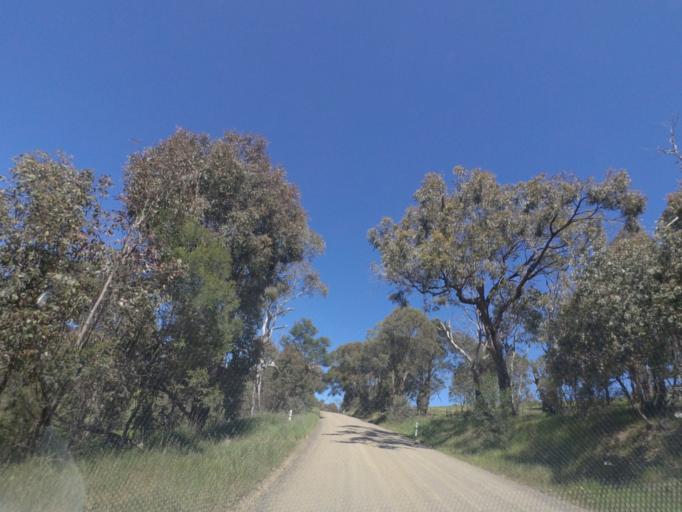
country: AU
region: Victoria
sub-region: Whittlesea
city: Whittlesea
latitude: -37.2823
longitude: 145.0091
